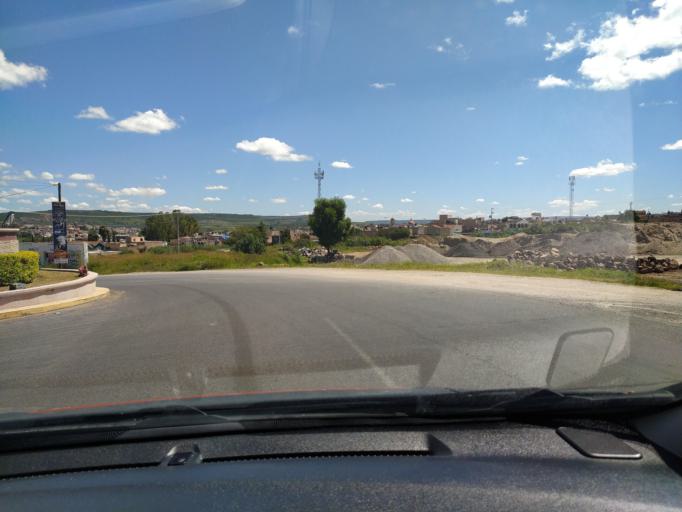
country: MX
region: Jalisco
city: San Miguel el Alto
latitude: 21.0290
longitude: -102.4132
